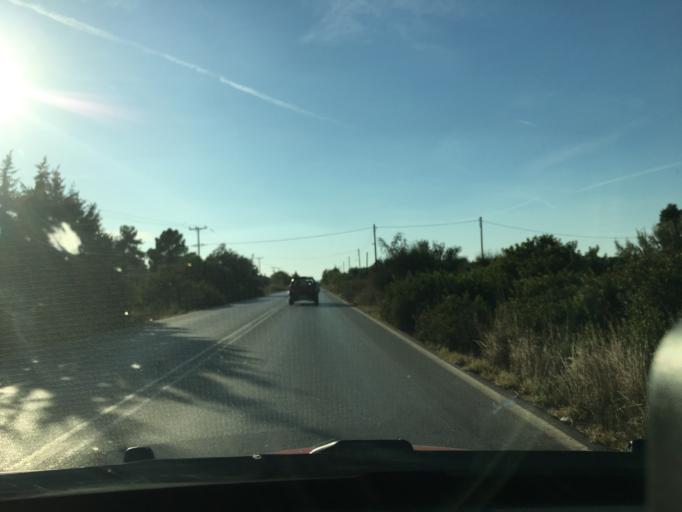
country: GR
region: Central Macedonia
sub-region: Nomos Chalkidikis
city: Kalyves Polygyrou
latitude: 40.2825
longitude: 23.4092
